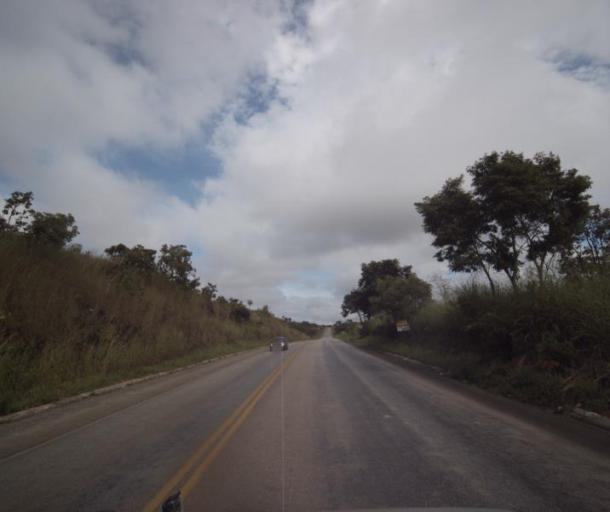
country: BR
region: Goias
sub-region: Pirenopolis
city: Pirenopolis
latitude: -15.7537
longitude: -48.7338
